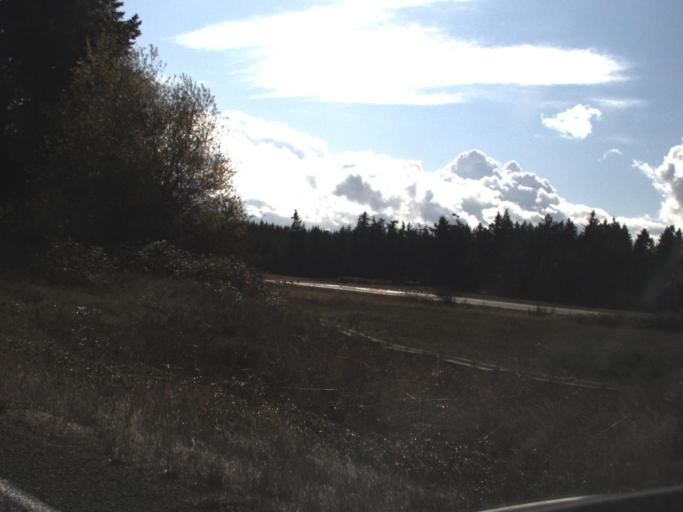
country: US
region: Washington
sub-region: Island County
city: Coupeville
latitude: 48.1833
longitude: -122.6263
